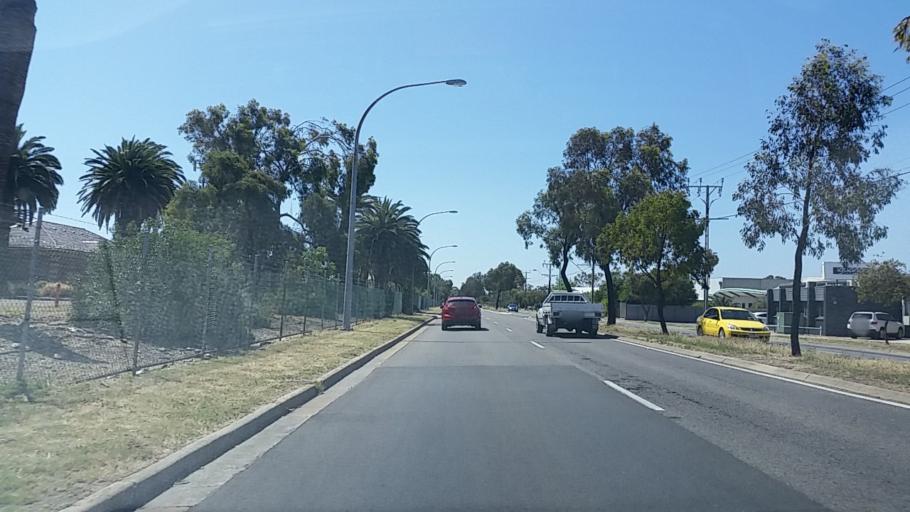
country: AU
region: South Australia
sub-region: Charles Sturt
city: Royal Park
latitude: -34.8655
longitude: 138.5026
